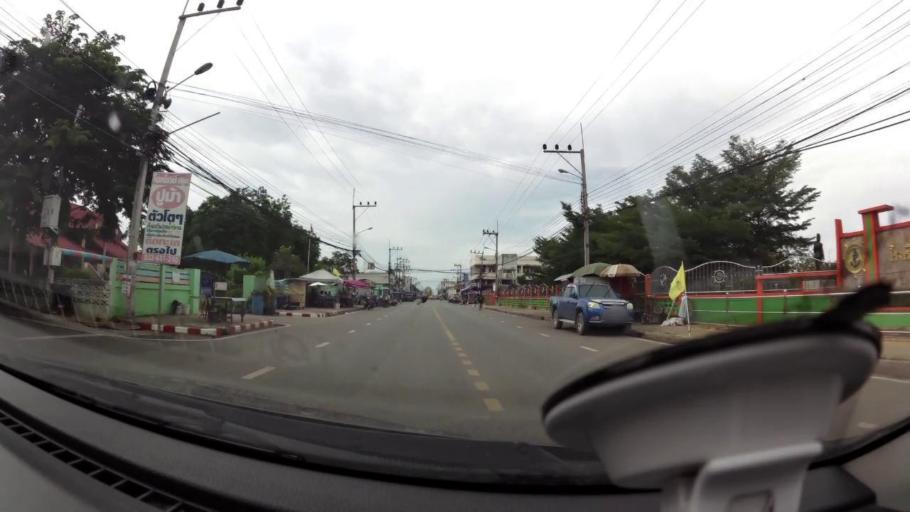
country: TH
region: Prachuap Khiri Khan
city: Pran Buri
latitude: 12.4010
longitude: 99.9912
